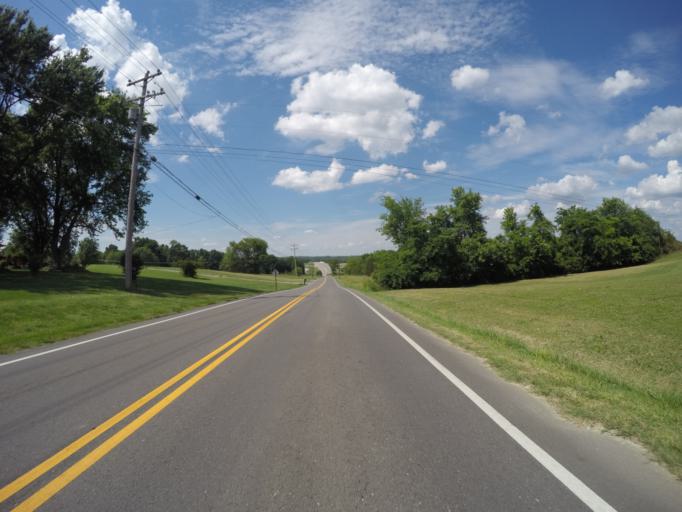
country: US
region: Tennessee
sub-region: Wilson County
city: Rural Hill
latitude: 36.1727
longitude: -86.4574
